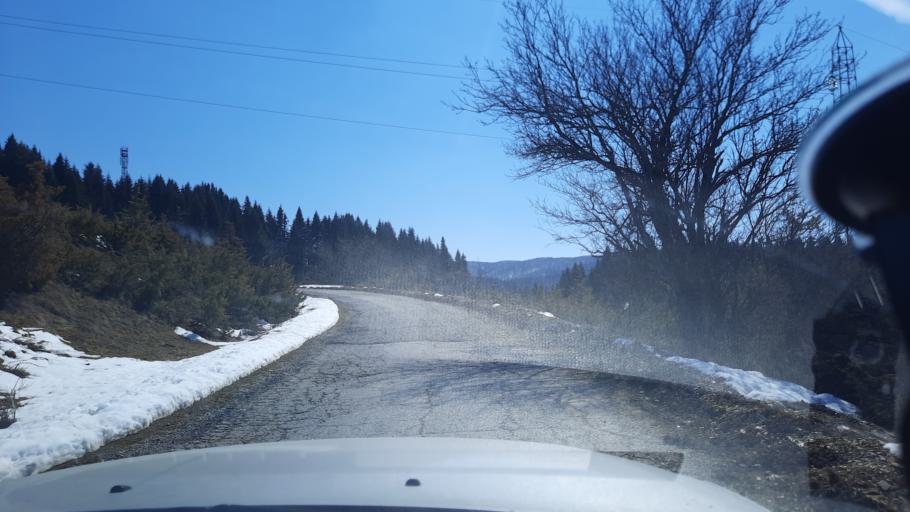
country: MK
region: Gostivar
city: Vrutok
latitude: 41.7153
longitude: 20.7255
